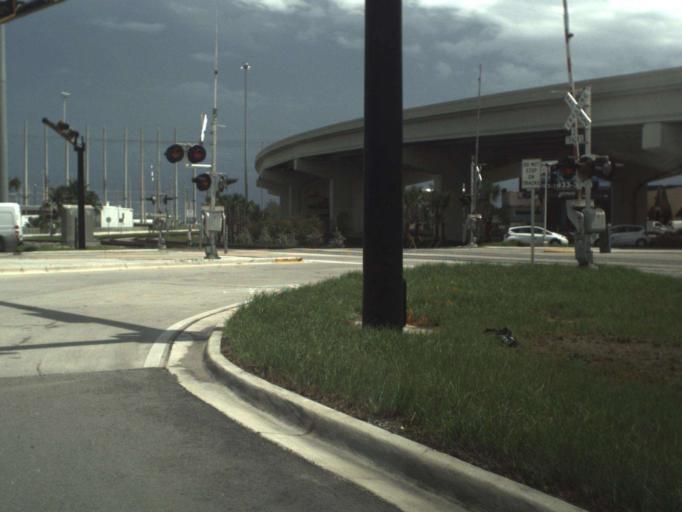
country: US
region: Florida
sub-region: Broward County
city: Dania Beach
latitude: 26.0820
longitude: -80.1308
